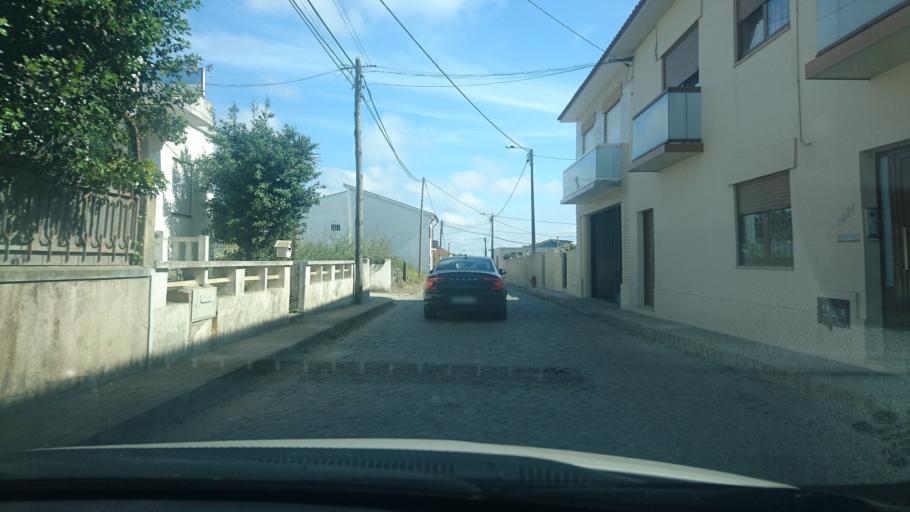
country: PT
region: Porto
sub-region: Matosinhos
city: Lavra
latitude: 41.2636
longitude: -8.7080
